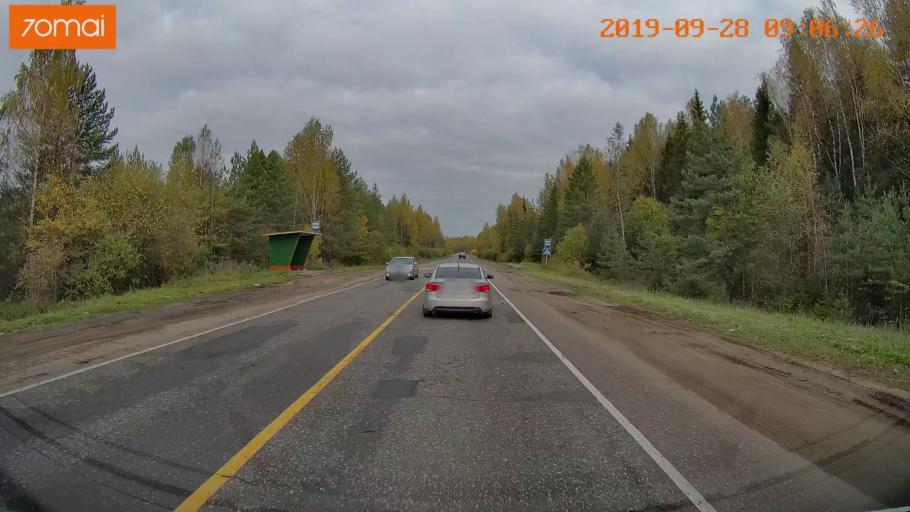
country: RU
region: Ivanovo
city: Pistsovo
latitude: 57.0824
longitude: 40.6734
